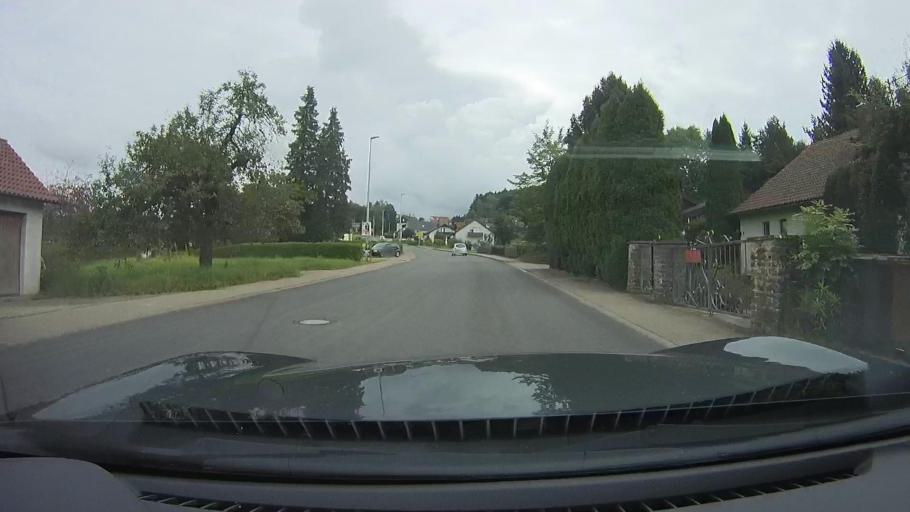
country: DE
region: Baden-Wuerttemberg
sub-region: Regierungsbezirk Stuttgart
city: Althutte
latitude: 48.9430
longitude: 9.5521
